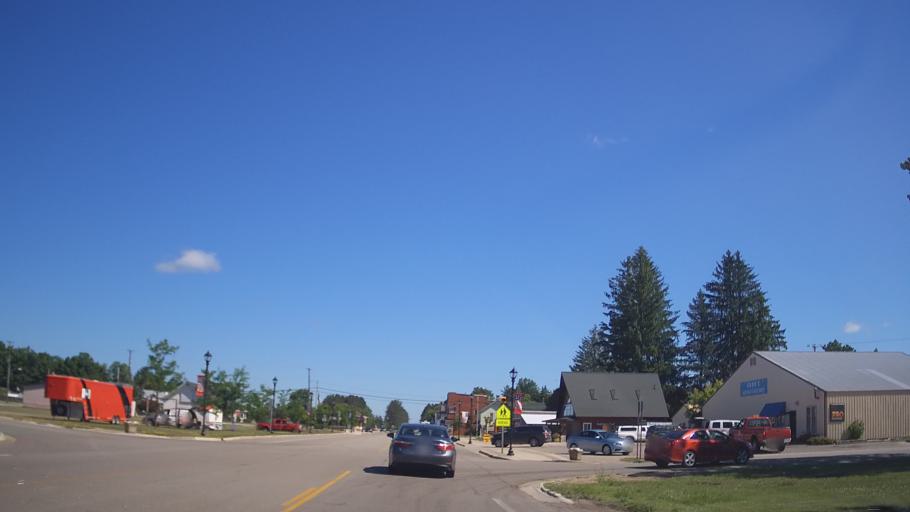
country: US
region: Michigan
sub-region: Cheboygan County
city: Indian River
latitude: 45.5507
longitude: -84.7845
